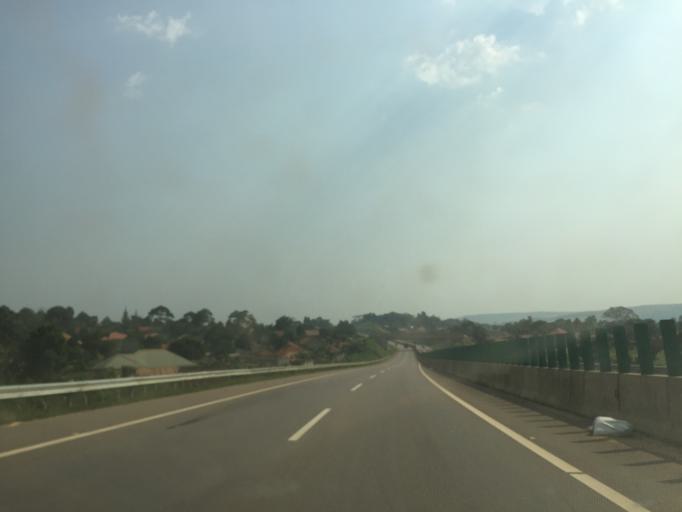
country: UG
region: Central Region
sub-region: Wakiso District
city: Kajansi
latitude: 0.2558
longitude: 32.5227
